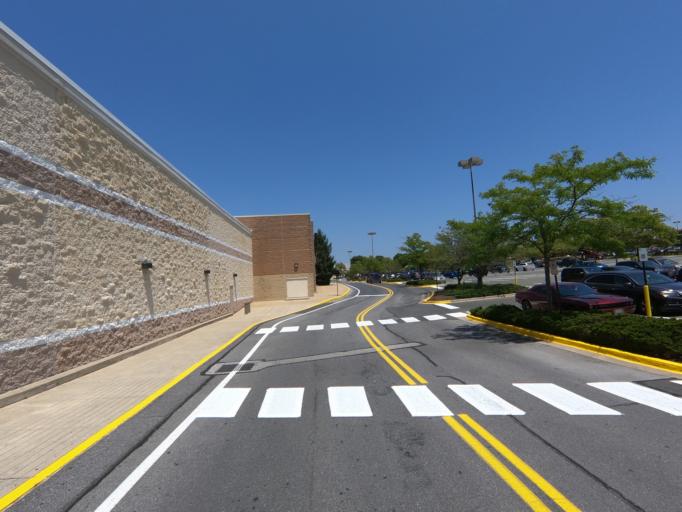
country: US
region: Maryland
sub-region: Montgomery County
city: Germantown
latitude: 39.1999
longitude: -77.2513
